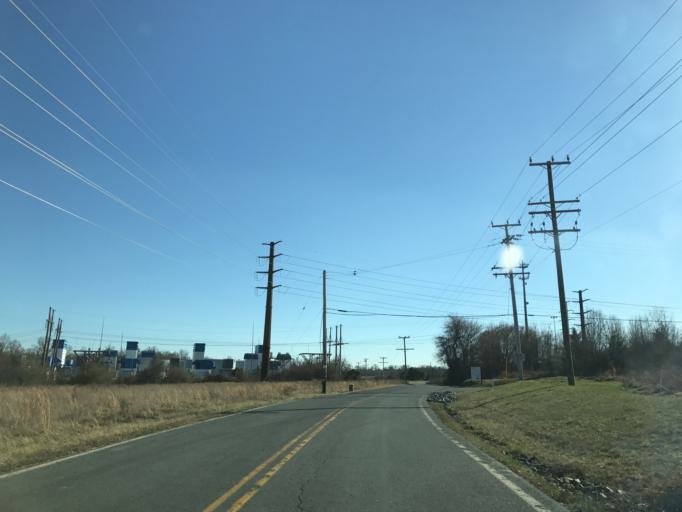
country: US
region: Maryland
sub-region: Harford County
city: Perryman
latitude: 39.4433
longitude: -76.2151
